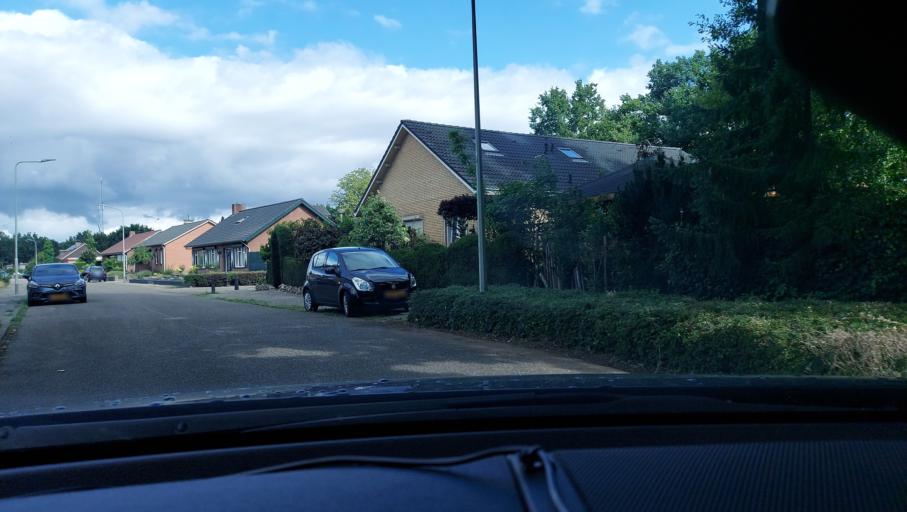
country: NL
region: Limburg
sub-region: Gemeente Beesel
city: Offenbeek
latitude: 51.2868
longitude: 6.0965
